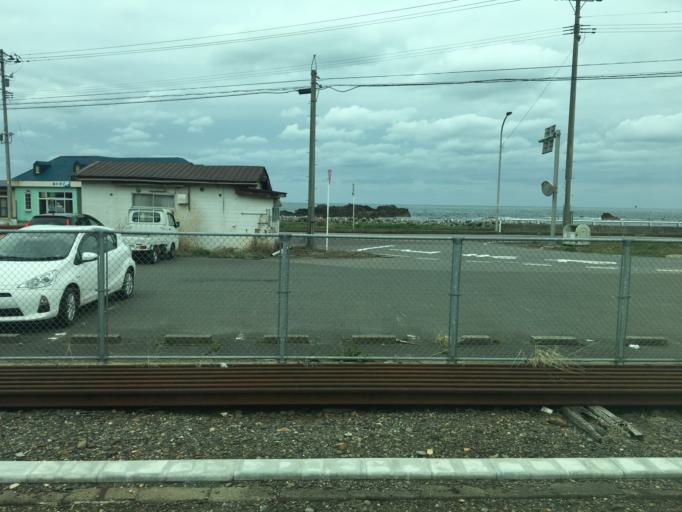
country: JP
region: Akita
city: Noshiromachi
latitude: 40.6505
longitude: 139.9294
